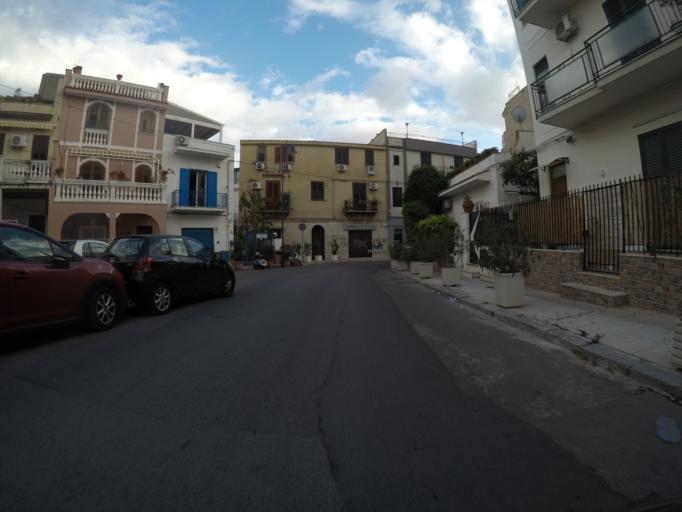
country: IT
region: Sicily
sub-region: Palermo
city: Palermo
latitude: 38.2086
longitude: 13.3274
